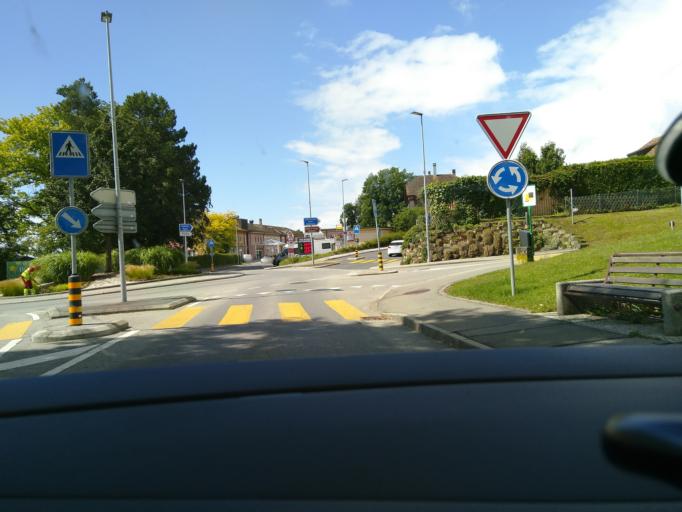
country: CH
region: Vaud
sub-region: Morges District
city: Aubonne
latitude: 46.4930
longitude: 6.3896
